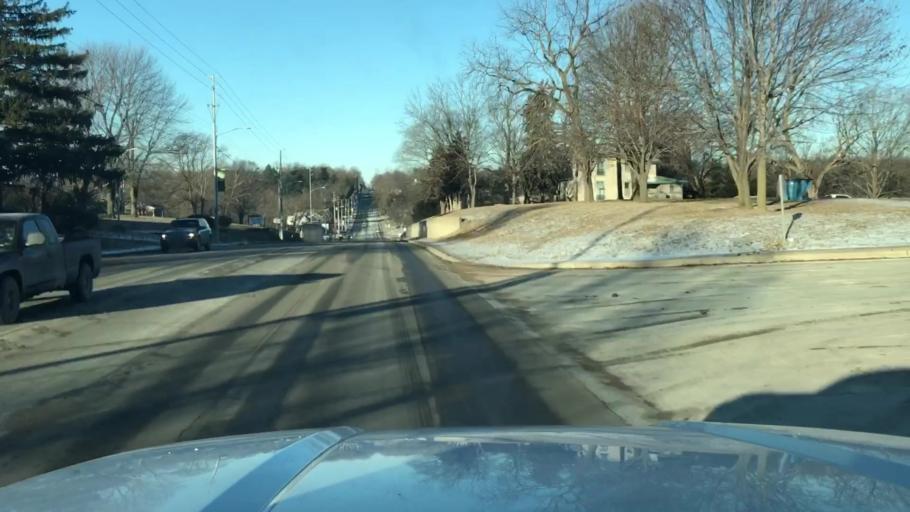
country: US
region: Missouri
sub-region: Buchanan County
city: Saint Joseph
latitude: 39.7770
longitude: -94.8125
